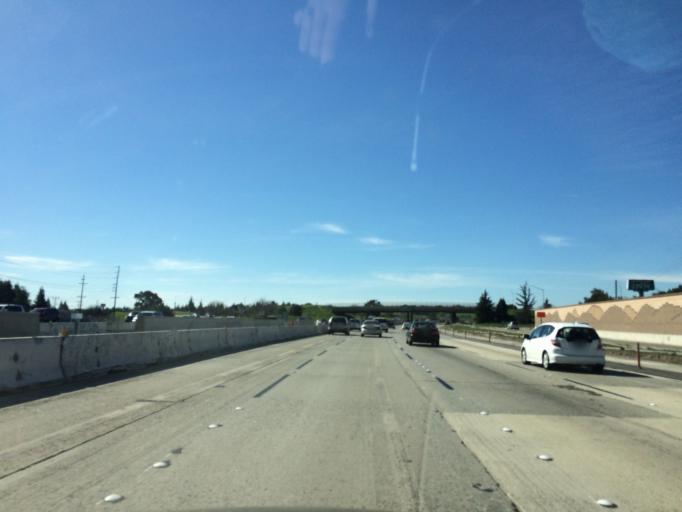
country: US
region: California
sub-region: Alameda County
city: Livermore
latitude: 37.7039
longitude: -121.7366
